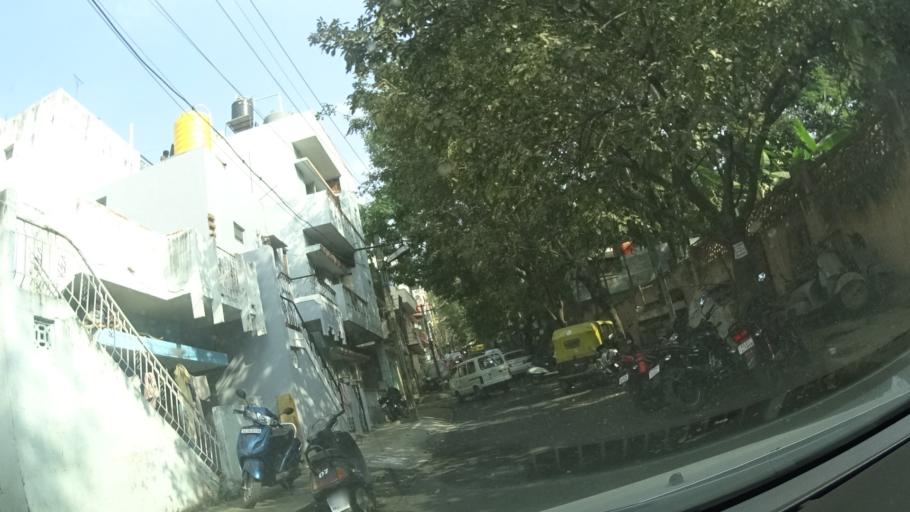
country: IN
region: Karnataka
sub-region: Bangalore Urban
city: Bangalore
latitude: 12.9494
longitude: 77.5632
